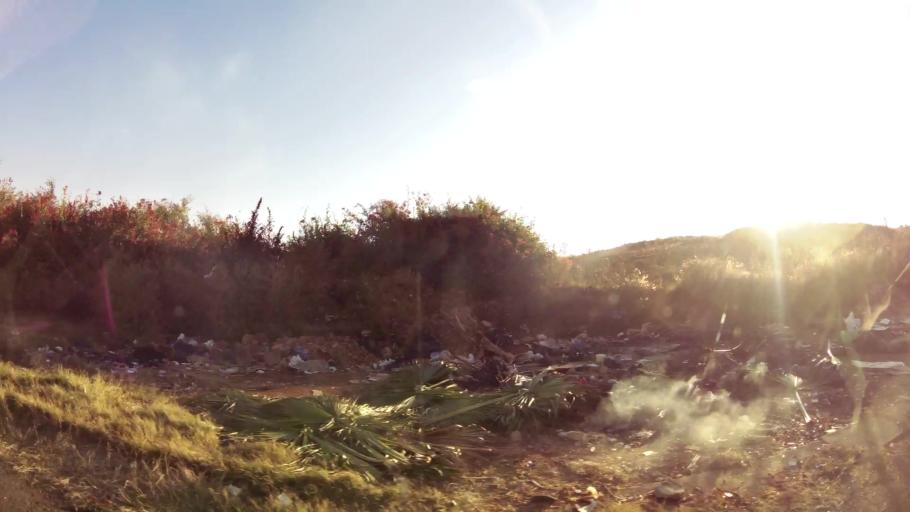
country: ZA
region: Gauteng
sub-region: City of Tshwane Metropolitan Municipality
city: Pretoria
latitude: -25.7329
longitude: 28.1162
